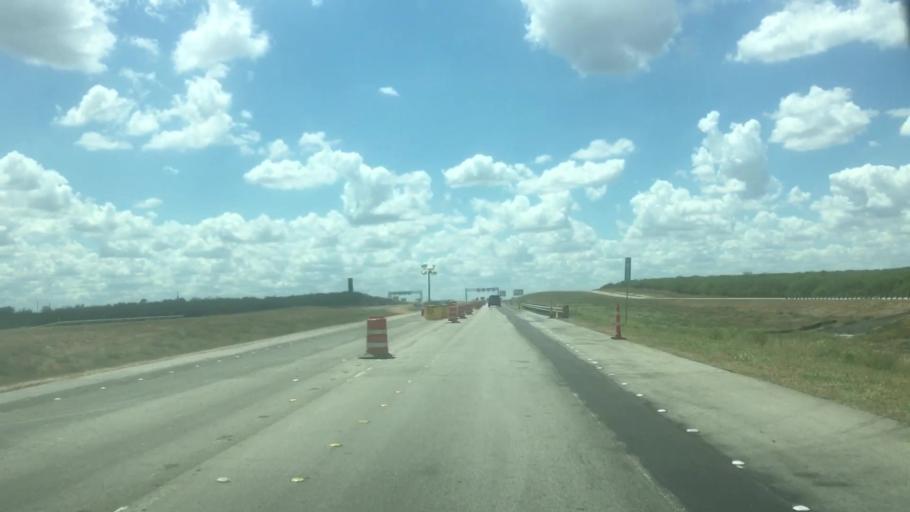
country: US
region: Texas
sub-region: Caldwell County
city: Martindale
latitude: 29.8185
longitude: -97.7575
